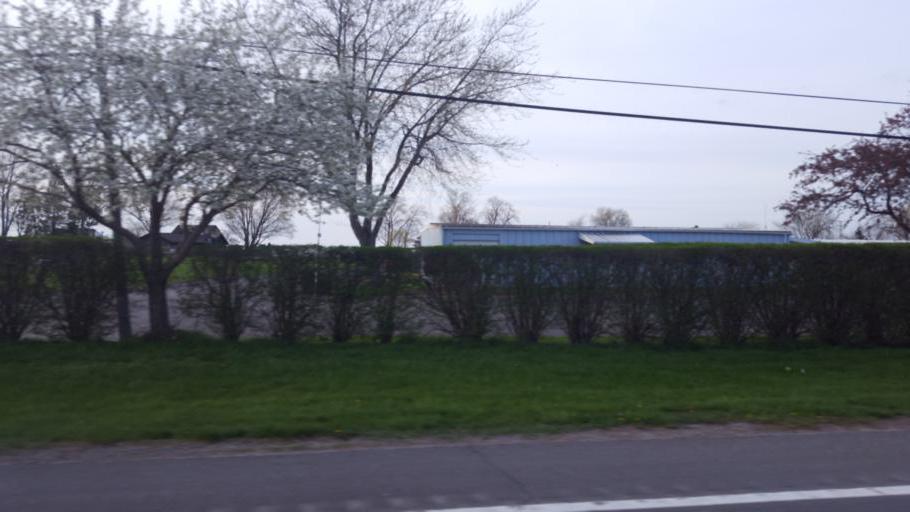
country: US
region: Ohio
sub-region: Erie County
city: Huron
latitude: 41.3789
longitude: -82.4850
